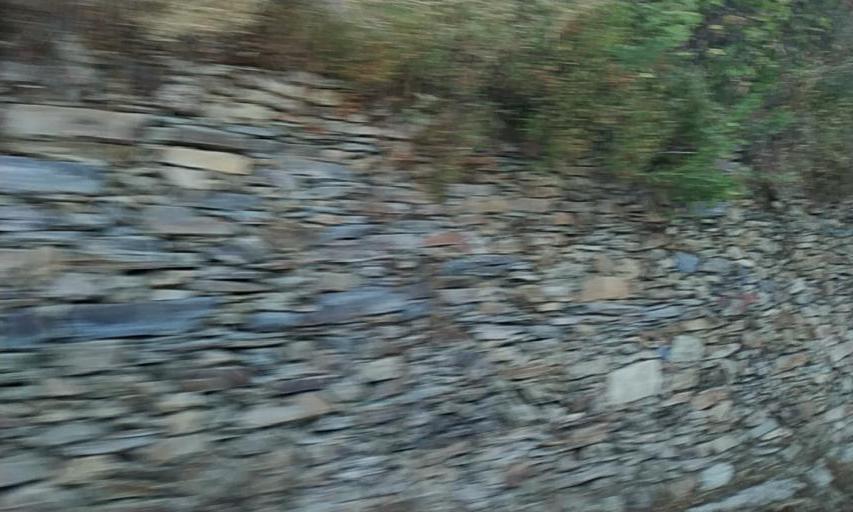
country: PT
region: Viseu
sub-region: Sao Joao da Pesqueira
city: Sao Joao da Pesqueira
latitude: 41.1849
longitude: -7.4191
